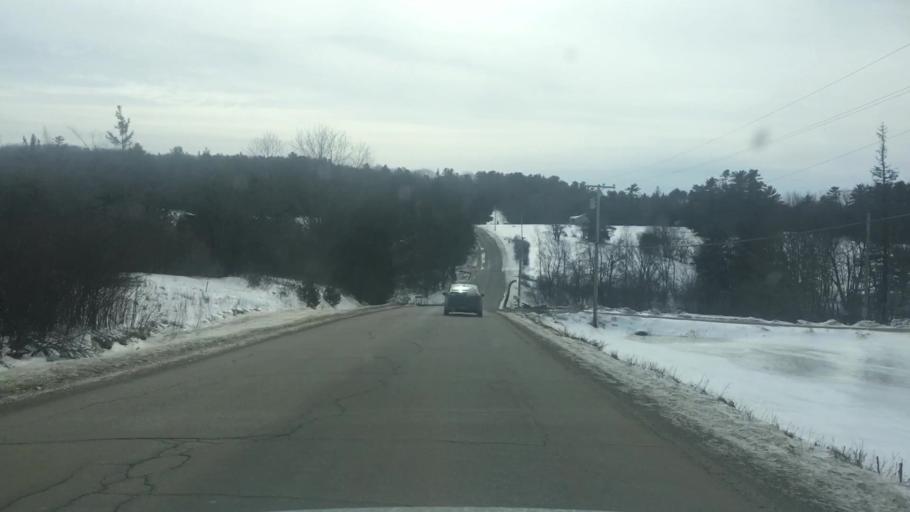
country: US
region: Maine
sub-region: Hancock County
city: Orland
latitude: 44.5950
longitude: -68.7243
